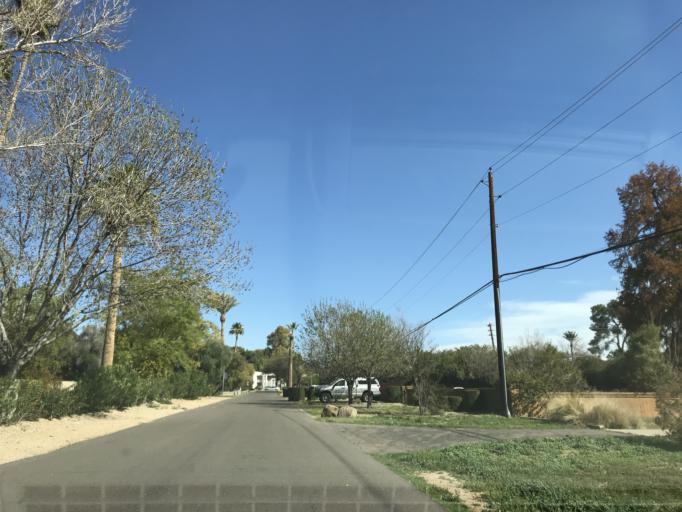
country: US
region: Arizona
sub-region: Maricopa County
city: Phoenix
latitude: 33.5130
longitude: -112.0322
